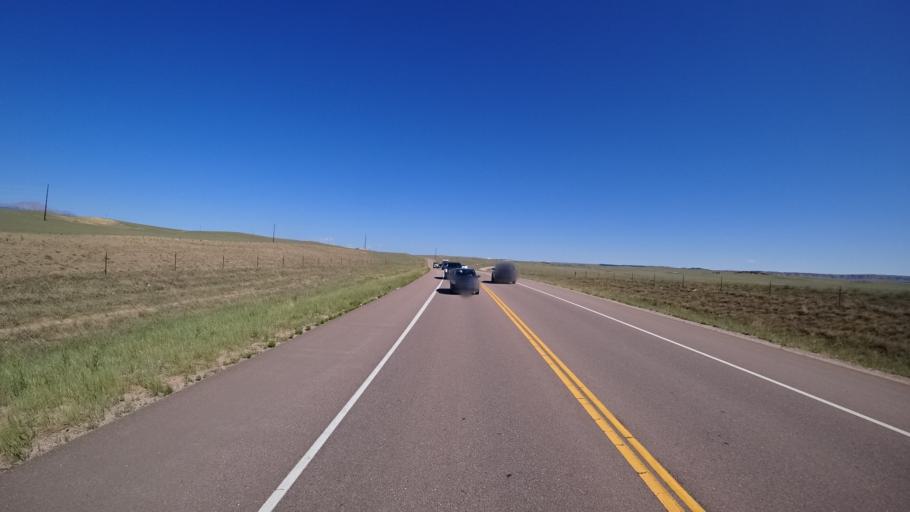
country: US
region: Colorado
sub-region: El Paso County
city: Security-Widefield
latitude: 38.7955
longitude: -104.6581
